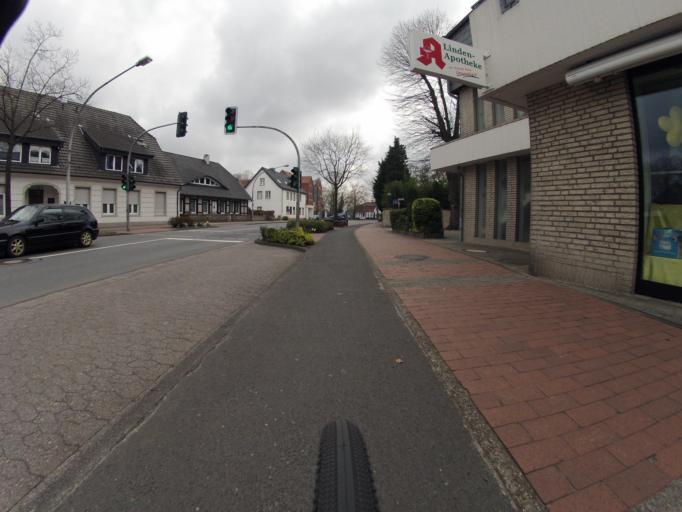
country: DE
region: North Rhine-Westphalia
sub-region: Regierungsbezirk Munster
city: Recke
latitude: 52.3685
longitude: 7.7196
